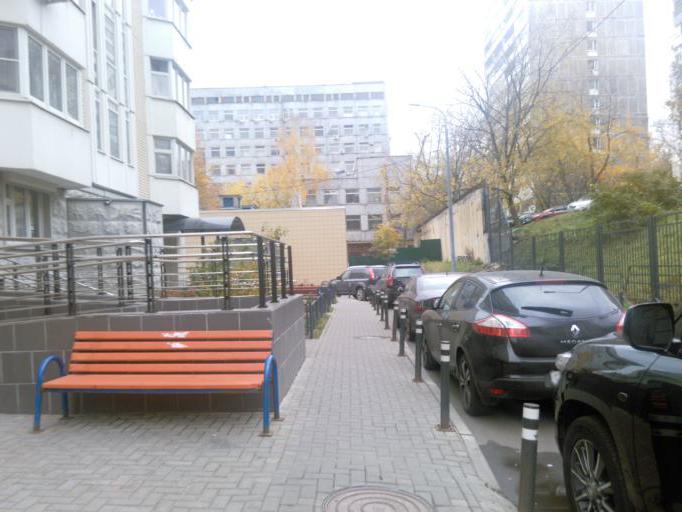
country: RU
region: Moscow
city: Mar'ina Roshcha
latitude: 55.8063
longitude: 37.6421
